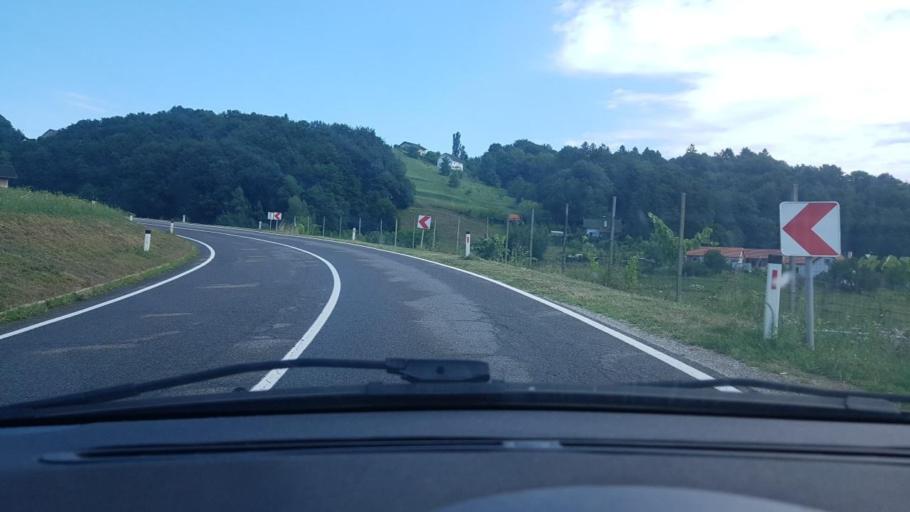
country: SI
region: Sentilj
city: Selnica ob Muri
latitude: 46.6893
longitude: 15.6922
